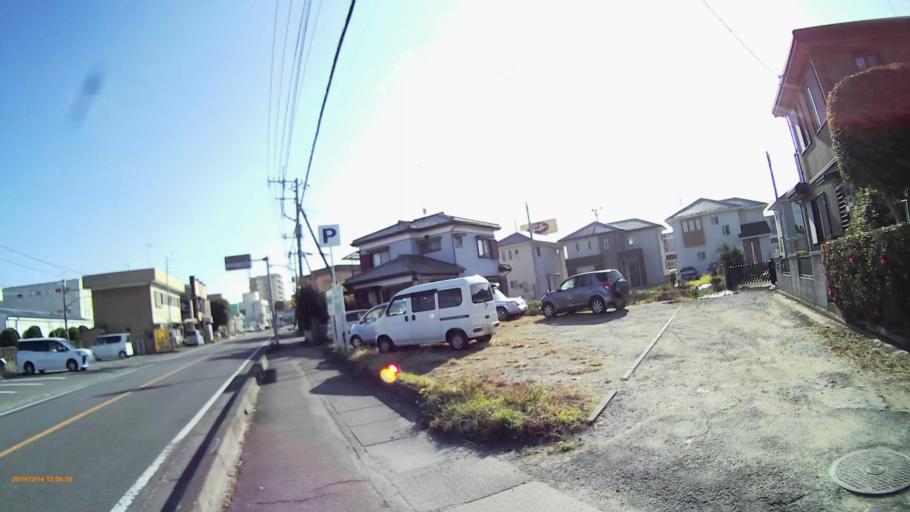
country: JP
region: Saitama
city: Fukiage-fujimi
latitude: 36.0987
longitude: 139.4609
